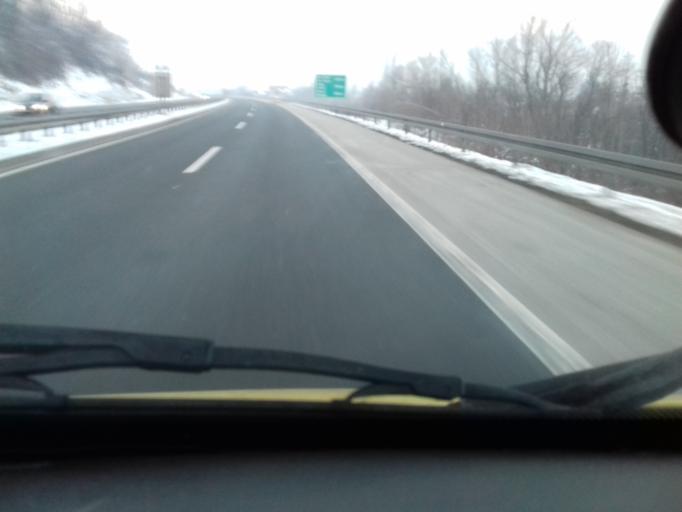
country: BA
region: Federation of Bosnia and Herzegovina
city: Vogosca
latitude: 43.9141
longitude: 18.3186
